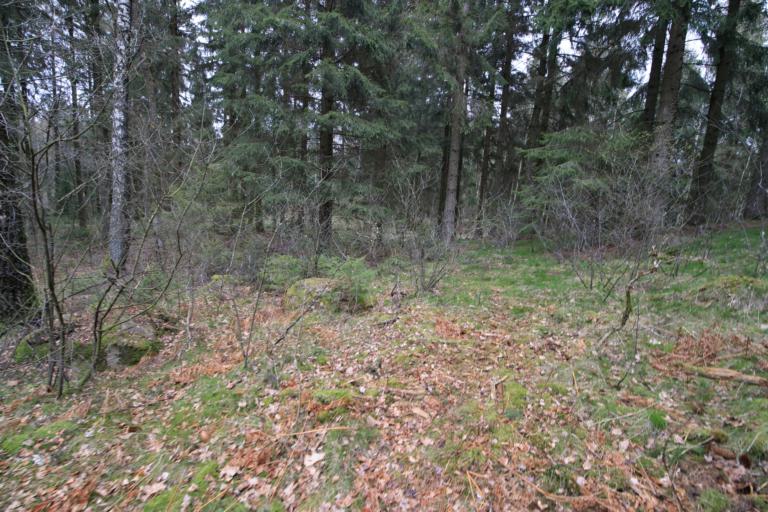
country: SE
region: Halland
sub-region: Varbergs Kommun
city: Tvaaker
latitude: 57.1500
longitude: 12.4563
